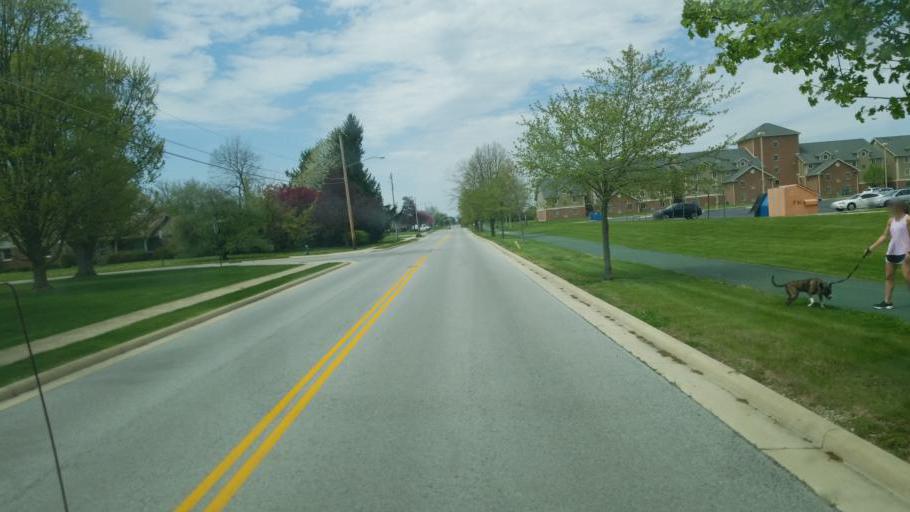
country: US
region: Ohio
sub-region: Hardin County
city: Ada
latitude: 40.7621
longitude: -83.8316
